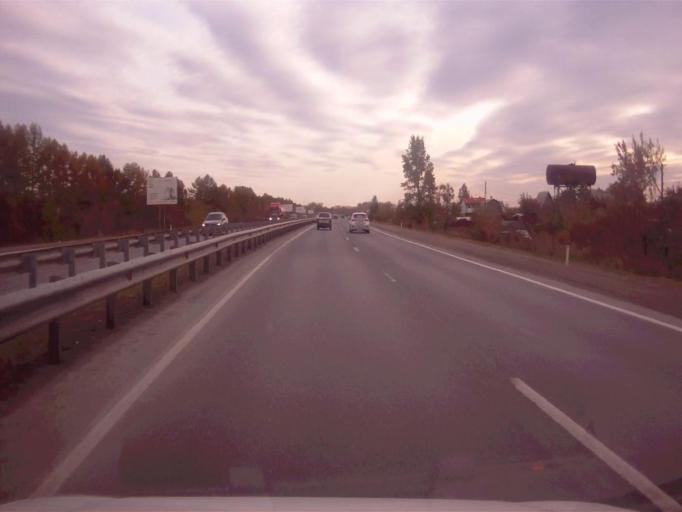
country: RU
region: Chelyabinsk
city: Novosineglazovskiy
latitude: 55.0267
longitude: 61.4499
